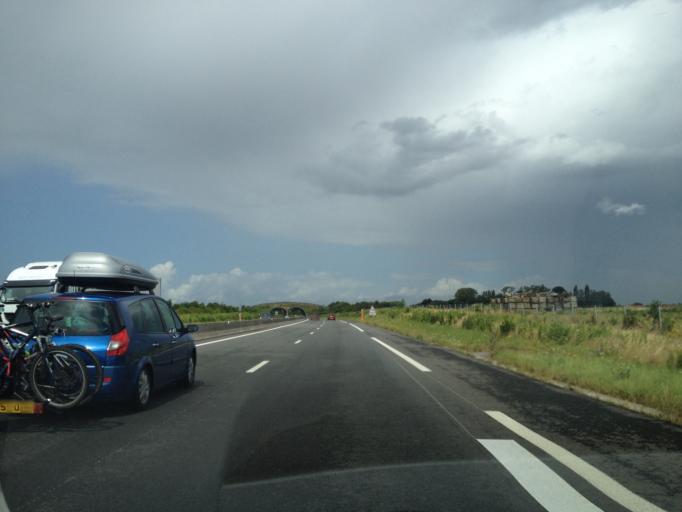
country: FR
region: Picardie
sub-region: Departement de la Somme
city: Nouvion
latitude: 50.2547
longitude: 1.7494
